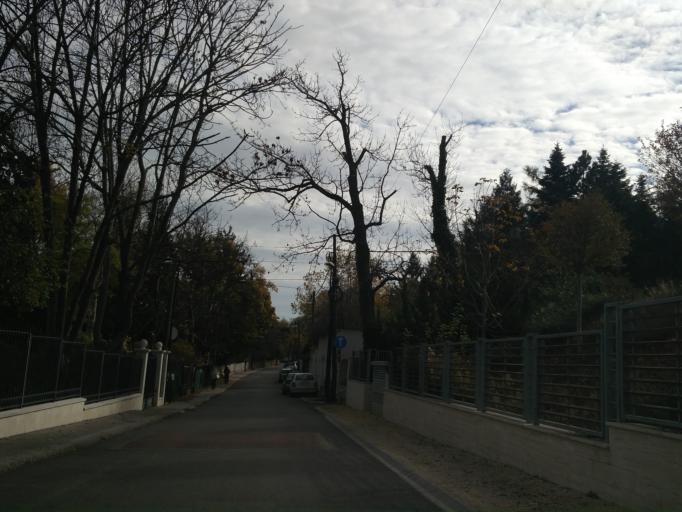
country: HU
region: Budapest
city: Budapest XII. keruelet
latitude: 47.5011
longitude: 18.9845
